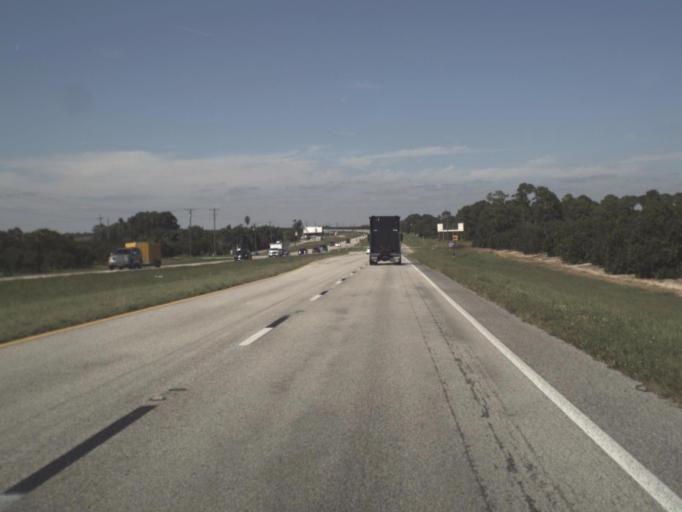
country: US
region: Florida
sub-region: Highlands County
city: Lake Placid
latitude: 27.3410
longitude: -81.3863
